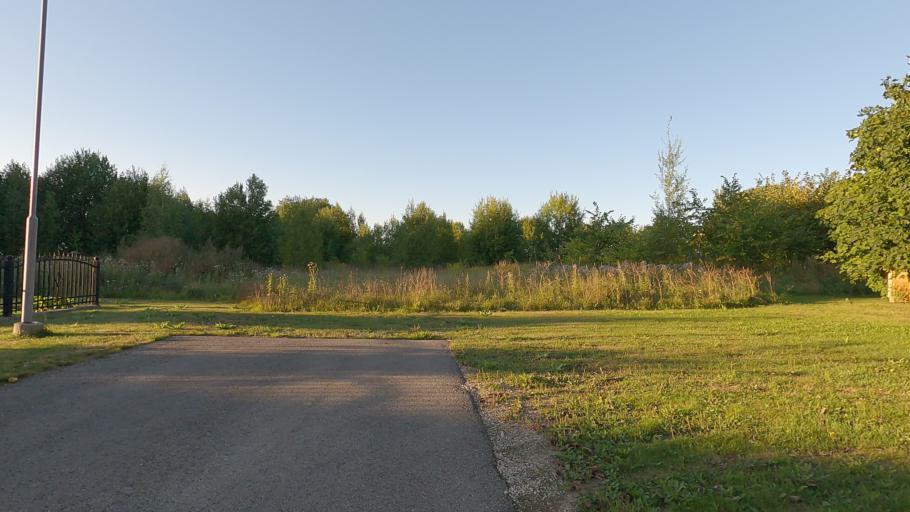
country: EE
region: Raplamaa
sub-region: Rapla vald
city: Rapla
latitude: 59.0053
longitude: 24.7813
